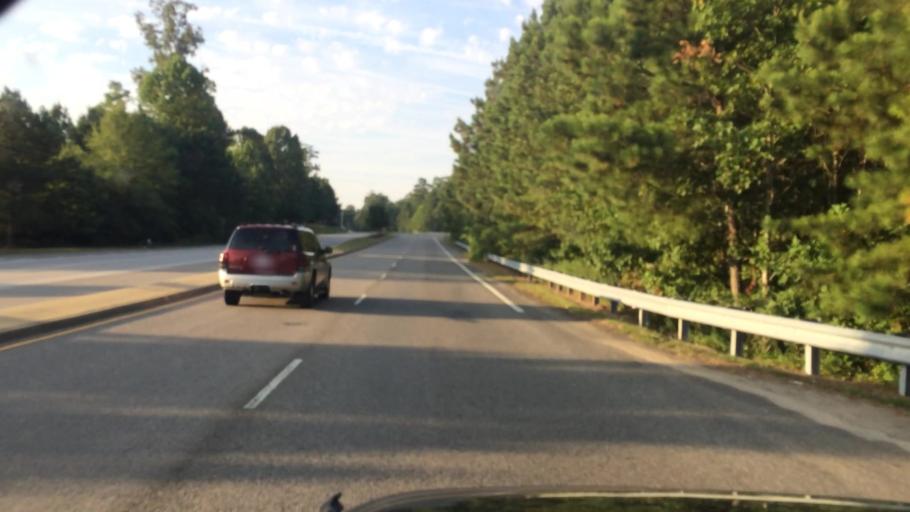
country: US
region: Virginia
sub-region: James City County
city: Williamsburg
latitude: 37.3364
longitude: -76.7373
